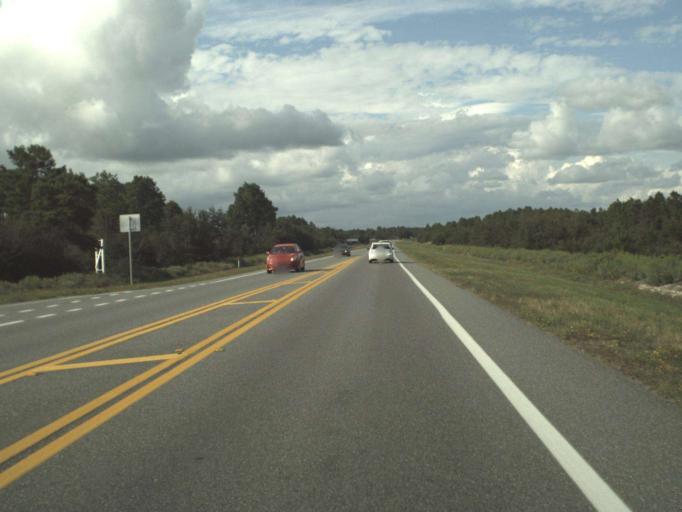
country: US
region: Florida
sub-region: Gulf County
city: Port Saint Joe
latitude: 29.8638
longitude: -85.3374
